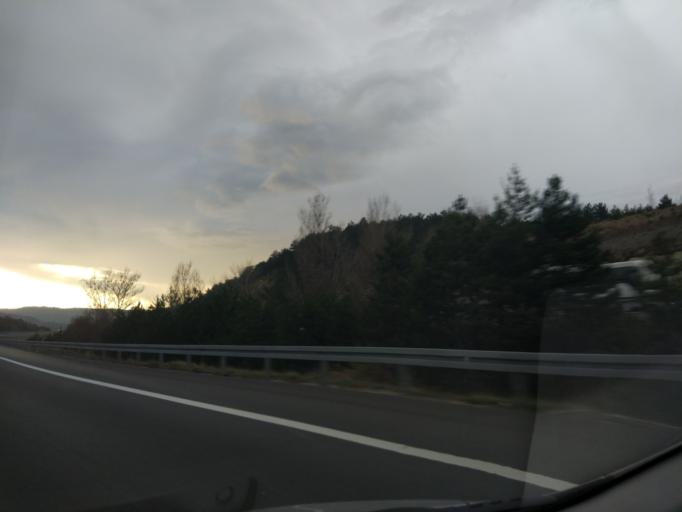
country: TR
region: Bolu
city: Yenicaga
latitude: 40.7494
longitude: 31.8964
